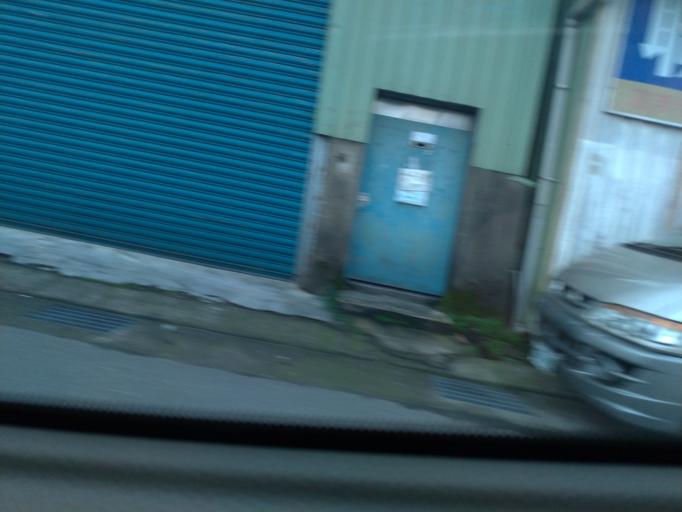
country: TW
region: Taiwan
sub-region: Taoyuan
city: Taoyuan
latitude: 24.9332
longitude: 121.3868
